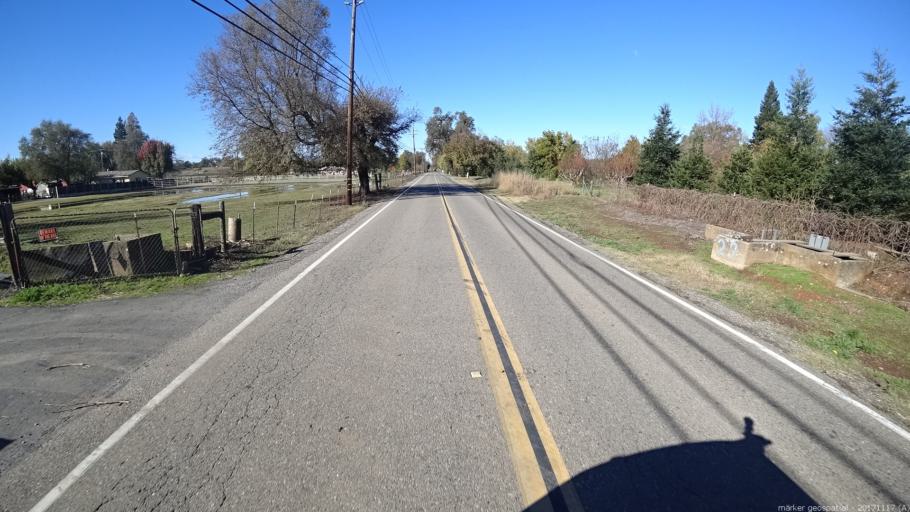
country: US
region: California
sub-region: Shasta County
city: Anderson
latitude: 40.4421
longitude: -122.2479
